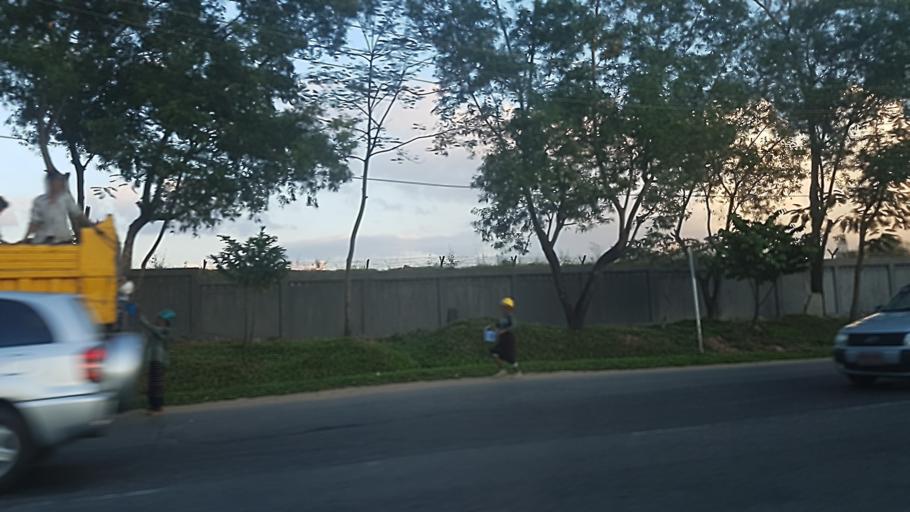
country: MM
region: Yangon
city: Yangon
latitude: 16.8993
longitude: 96.1239
